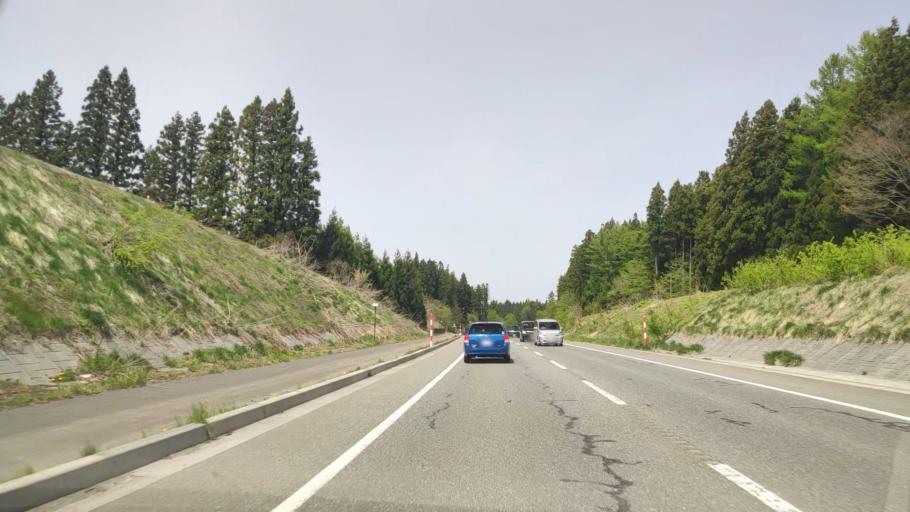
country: JP
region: Aomori
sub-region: Misawa Shi
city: Inuotose
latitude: 40.6858
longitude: 141.1701
